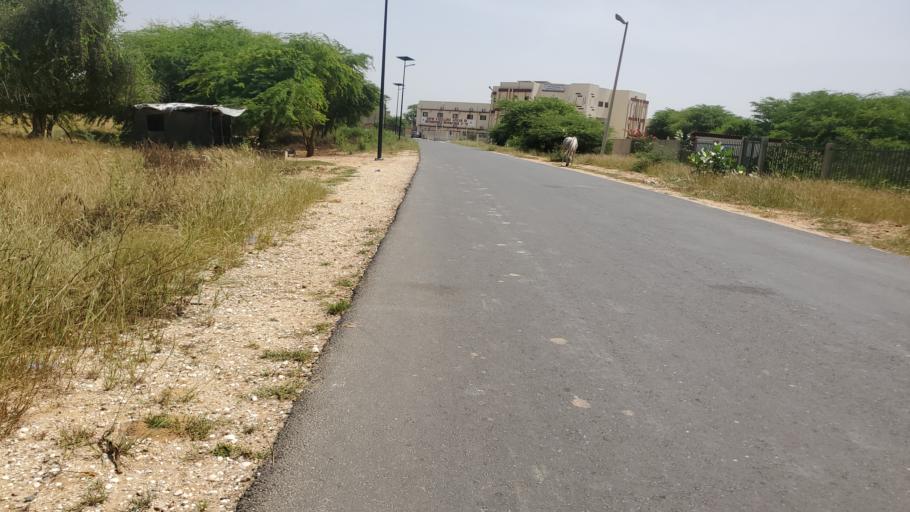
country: SN
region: Saint-Louis
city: Saint-Louis
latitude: 16.0574
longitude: -16.4273
